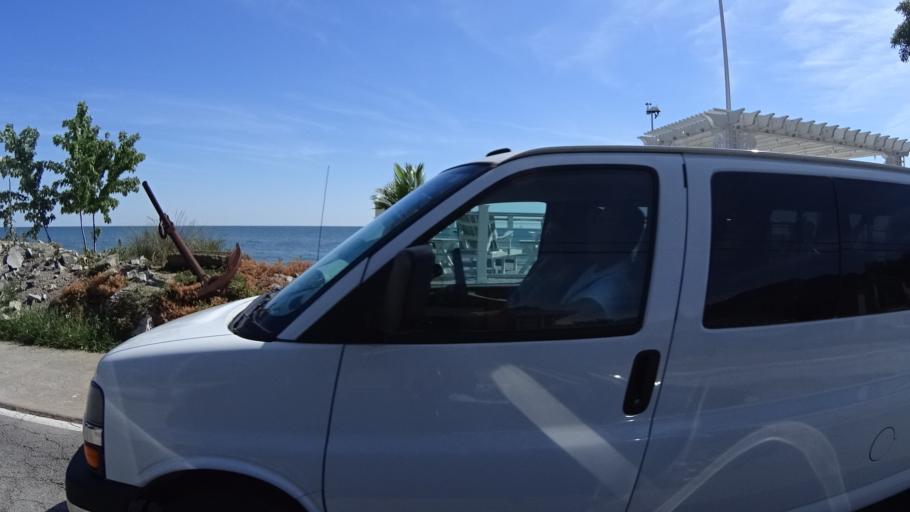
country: US
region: Ohio
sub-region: Erie County
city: Sandusky
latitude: 41.4699
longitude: -82.6680
